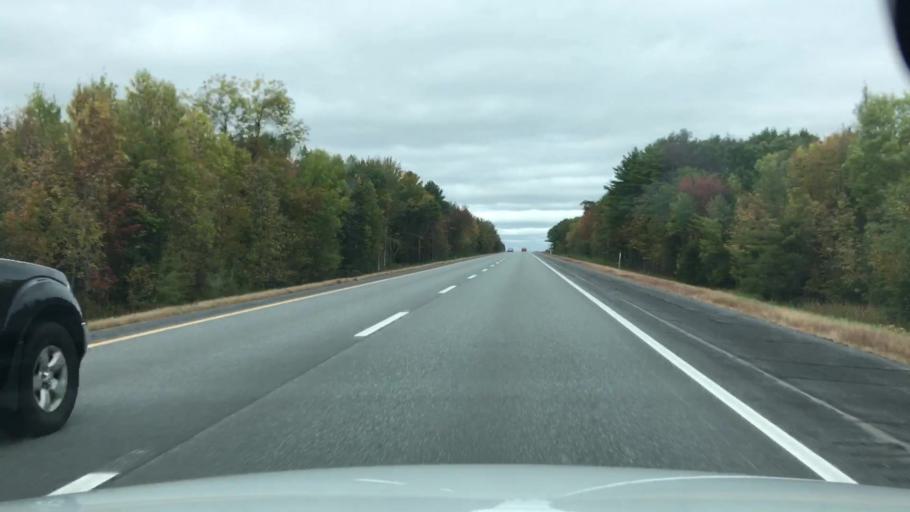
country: US
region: Maine
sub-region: Somerset County
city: Pittsfield
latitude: 44.7577
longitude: -69.4172
